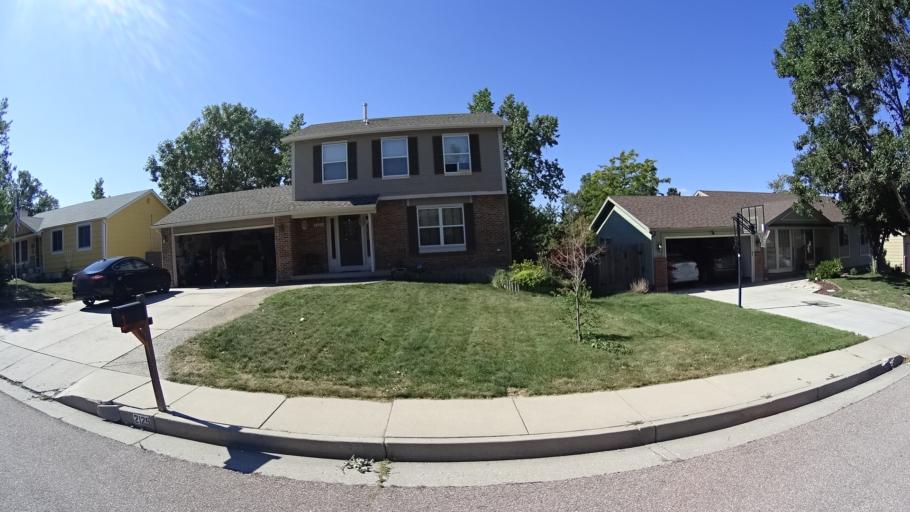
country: US
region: Colorado
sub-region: El Paso County
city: Air Force Academy
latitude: 38.9407
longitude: -104.7862
